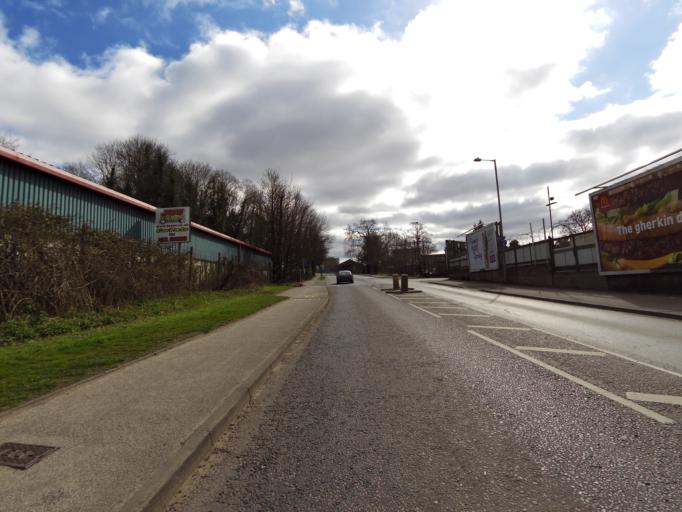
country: GB
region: England
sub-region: Suffolk
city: Ipswich
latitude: 52.0459
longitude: 1.1661
